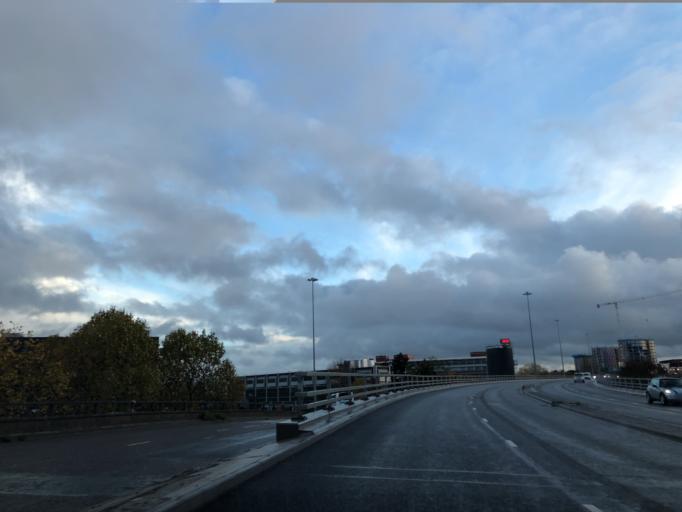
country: GB
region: England
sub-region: Coventry
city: Coventry
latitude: 52.4094
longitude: -1.5027
